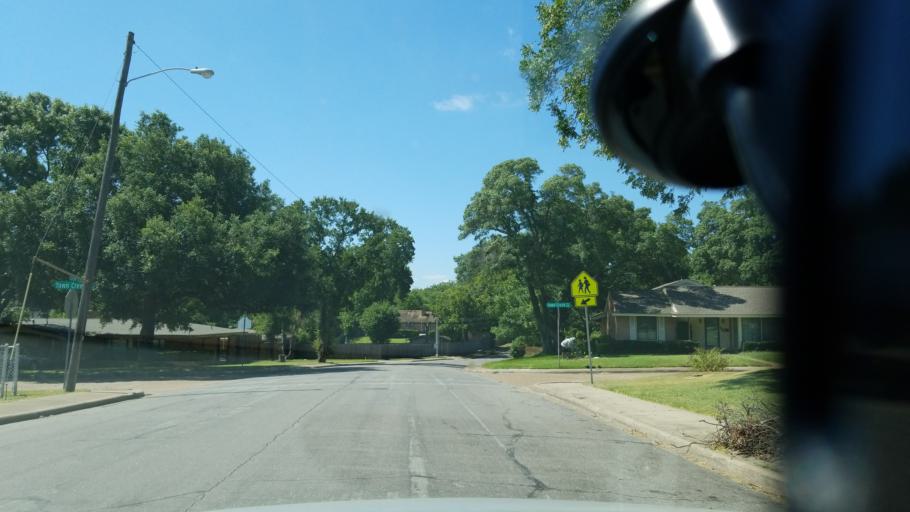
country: US
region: Texas
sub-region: Dallas County
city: Cockrell Hill
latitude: 32.6834
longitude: -96.8345
